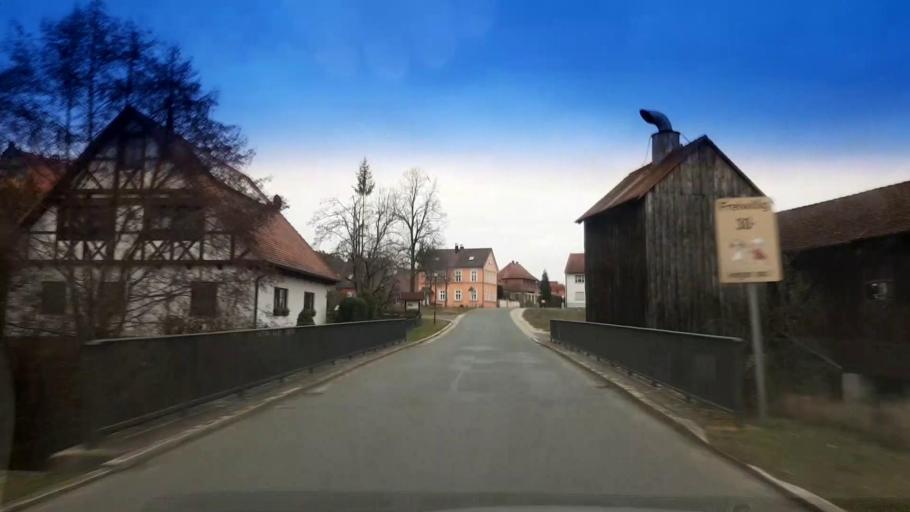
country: DE
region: Bavaria
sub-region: Upper Franconia
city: Pettstadt
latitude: 49.7913
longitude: 10.9080
